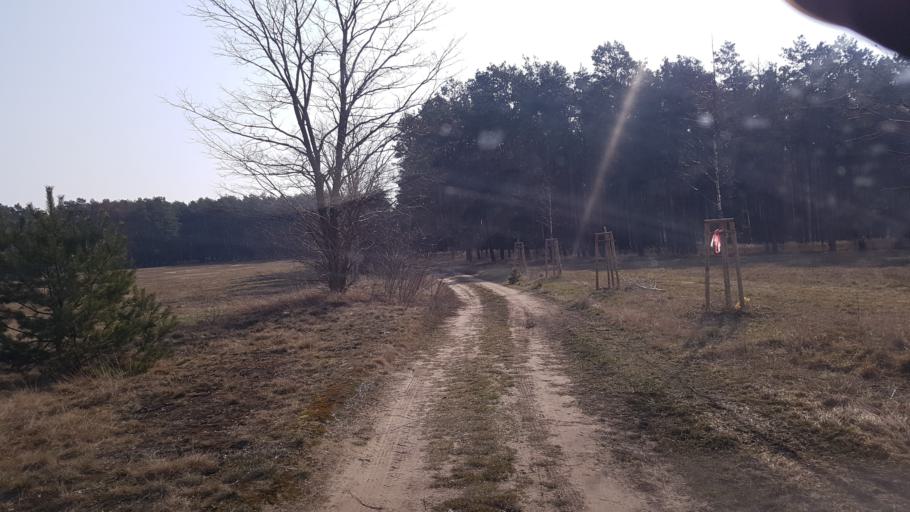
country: DE
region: Brandenburg
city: Schlieben
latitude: 51.6737
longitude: 13.3116
